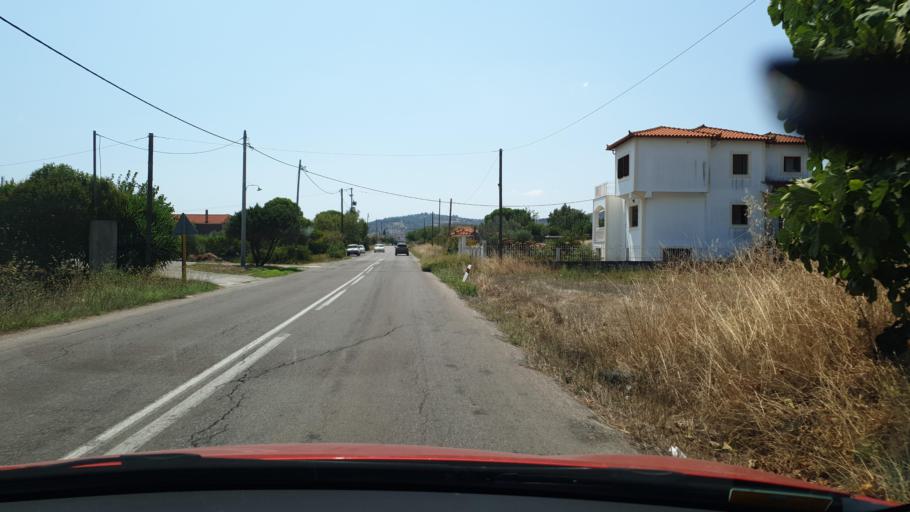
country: GR
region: Central Greece
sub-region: Nomos Evvoias
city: Aliveri
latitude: 38.4618
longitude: 24.1167
